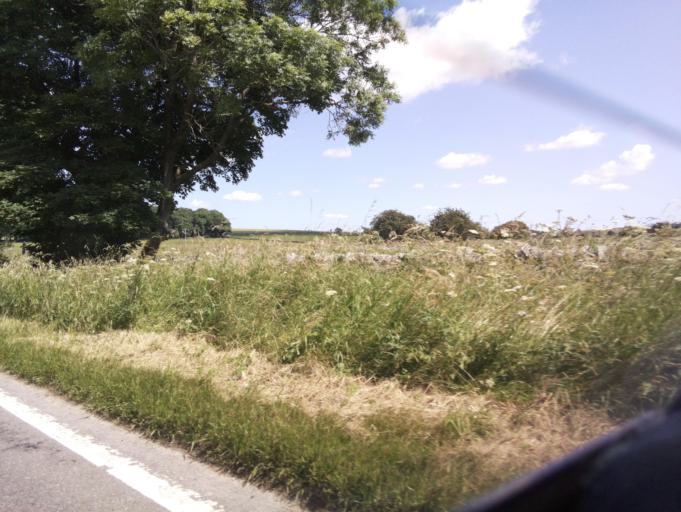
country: GB
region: England
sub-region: Derbyshire
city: Ashbourne
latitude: 53.1175
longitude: -1.7537
